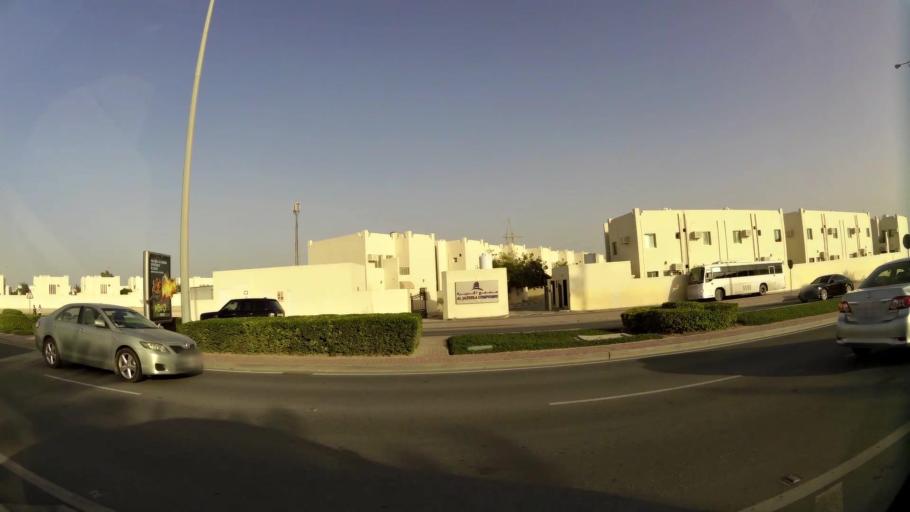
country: QA
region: Baladiyat ar Rayyan
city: Ar Rayyan
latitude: 25.3296
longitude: 51.4617
